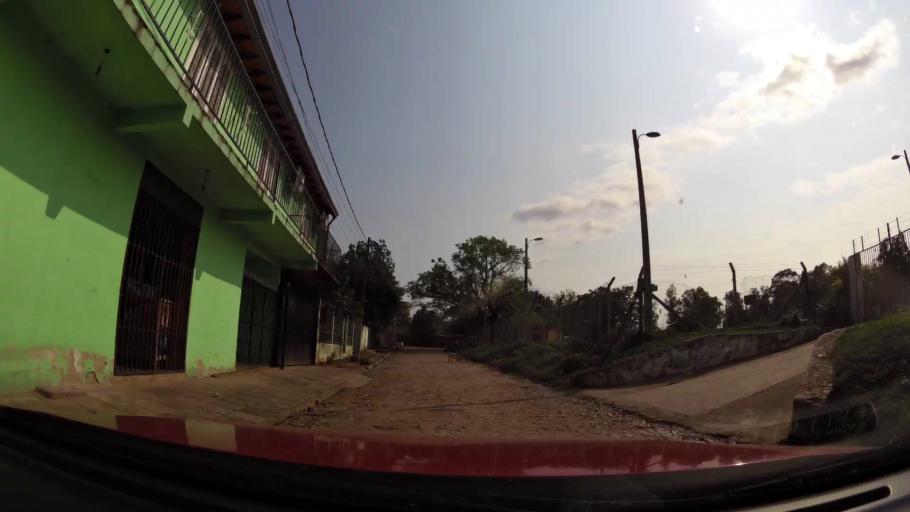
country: PY
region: Asuncion
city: Asuncion
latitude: -25.3004
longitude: -57.6637
